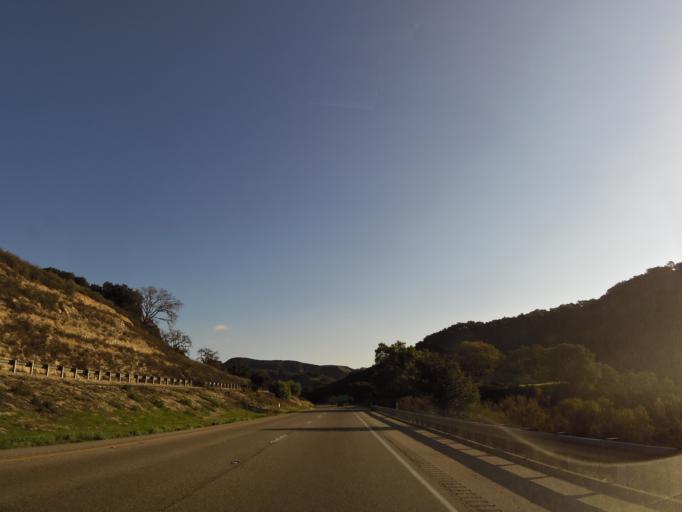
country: US
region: California
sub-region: Santa Barbara County
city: Los Olivos
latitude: 34.6693
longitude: -120.1678
